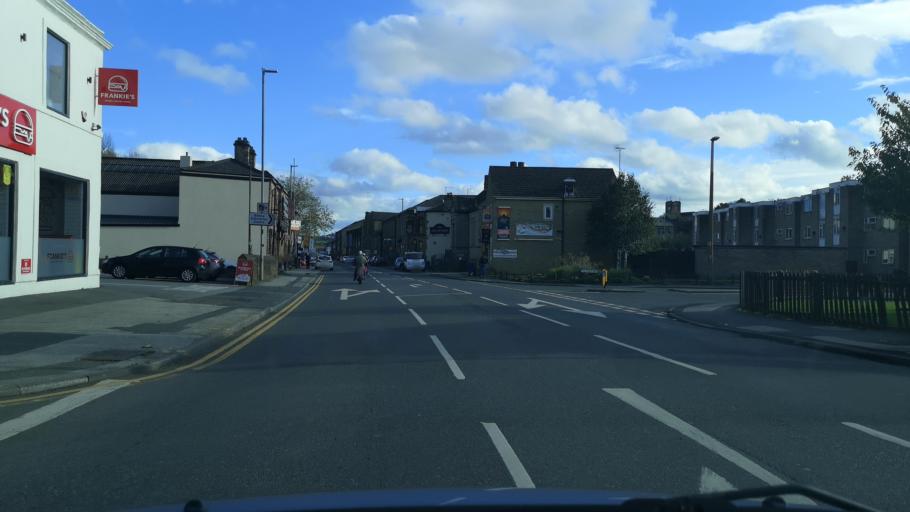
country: GB
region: England
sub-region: Kirklees
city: Batley
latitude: 53.7201
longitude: -1.6427
